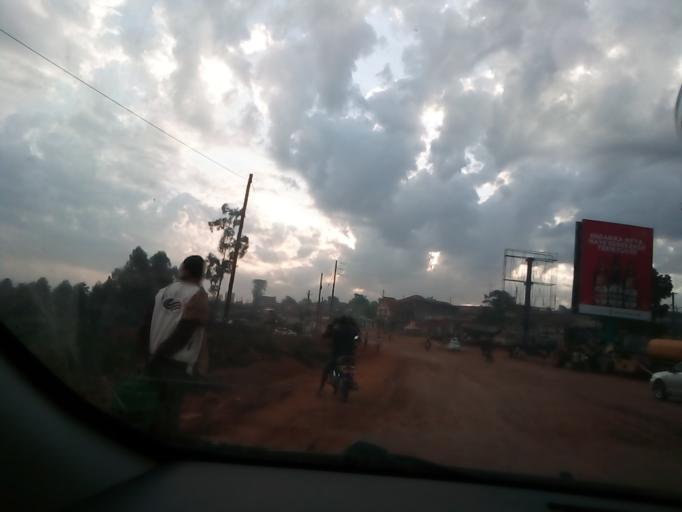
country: UG
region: Central Region
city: Masaka
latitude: -0.3278
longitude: 31.7506
